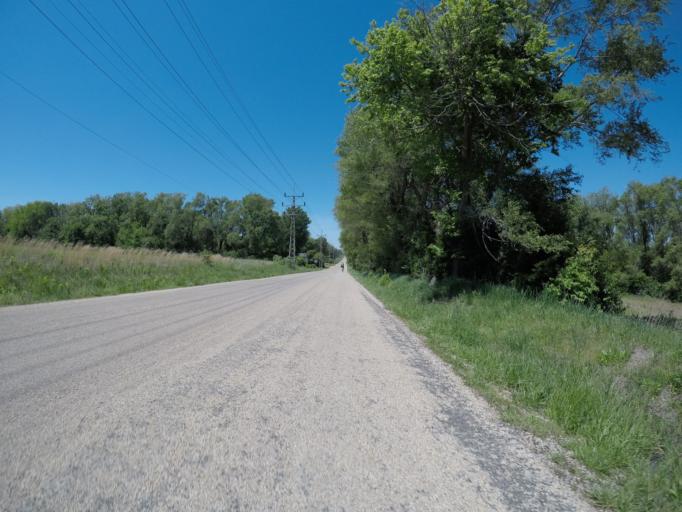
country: US
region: Kansas
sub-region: Shawnee County
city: Topeka
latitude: 39.0516
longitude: -95.6076
